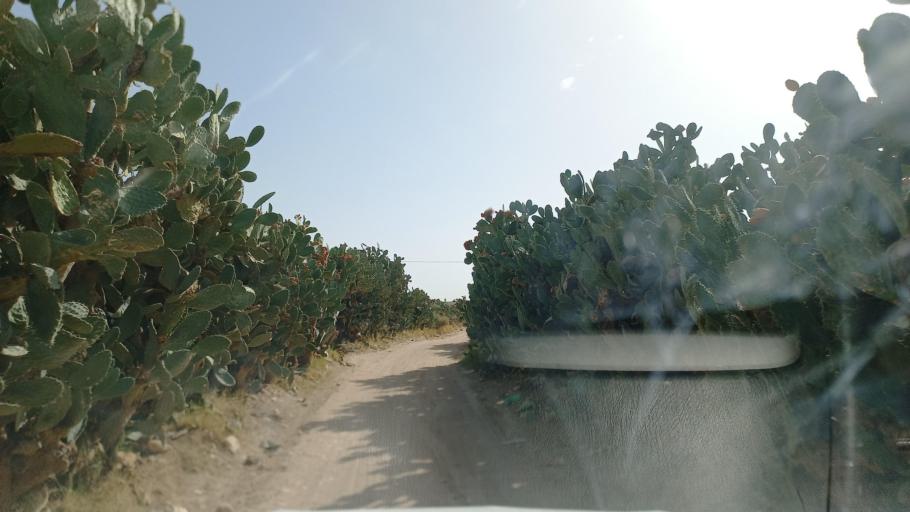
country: TN
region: Al Qasrayn
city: Kasserine
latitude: 35.2711
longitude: 8.9386
